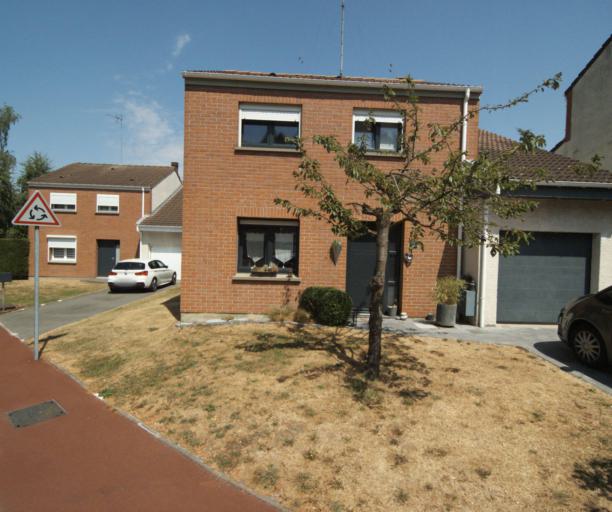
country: FR
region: Nord-Pas-de-Calais
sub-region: Departement du Nord
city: Neuville-en-Ferrain
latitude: 50.7479
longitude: 3.1688
